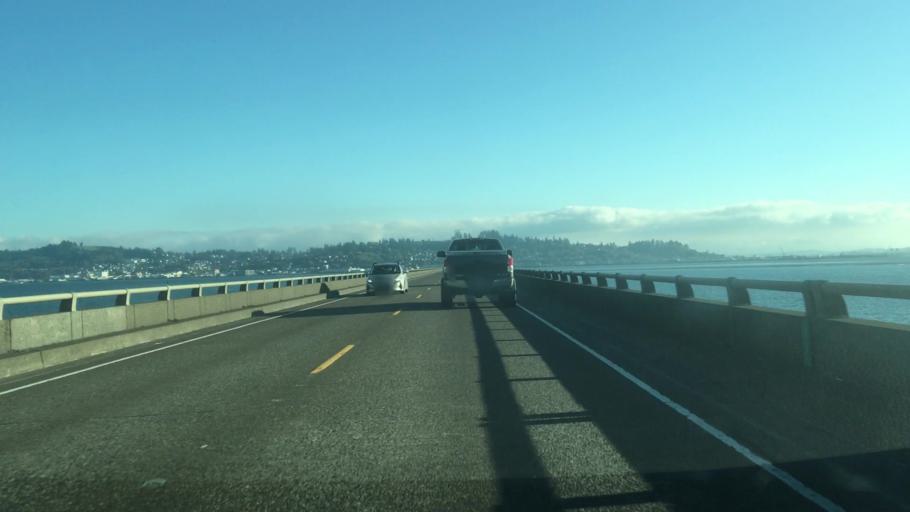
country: US
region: Oregon
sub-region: Clatsop County
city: Astoria
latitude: 46.2160
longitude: -123.8622
